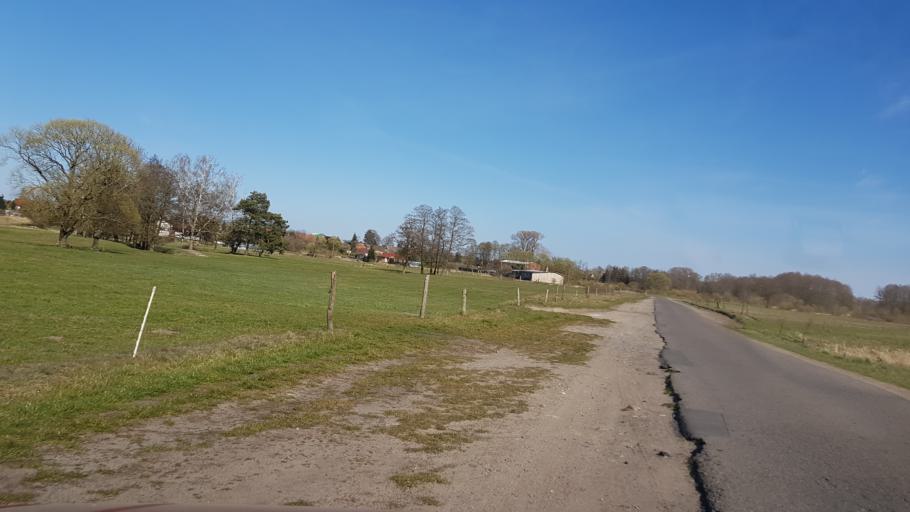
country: PL
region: West Pomeranian Voivodeship
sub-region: Powiat stargardzki
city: Stargard Szczecinski
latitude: 53.3807
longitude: 15.0007
